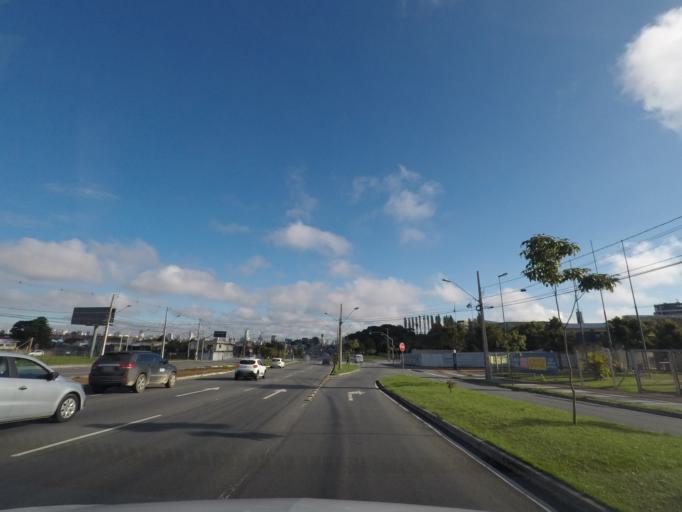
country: BR
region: Parana
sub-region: Curitiba
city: Curitiba
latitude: -25.4513
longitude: -49.2435
